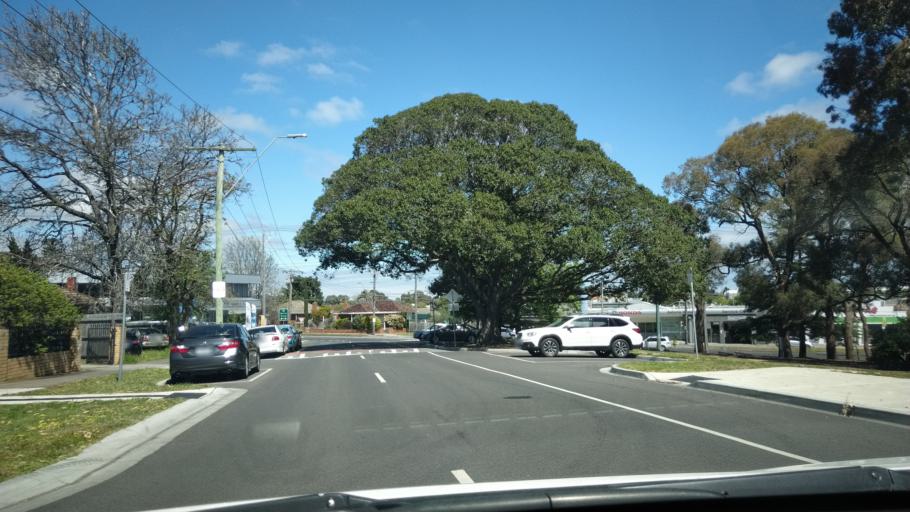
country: AU
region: Victoria
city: Murrumbeena
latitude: -37.9062
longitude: 145.0660
